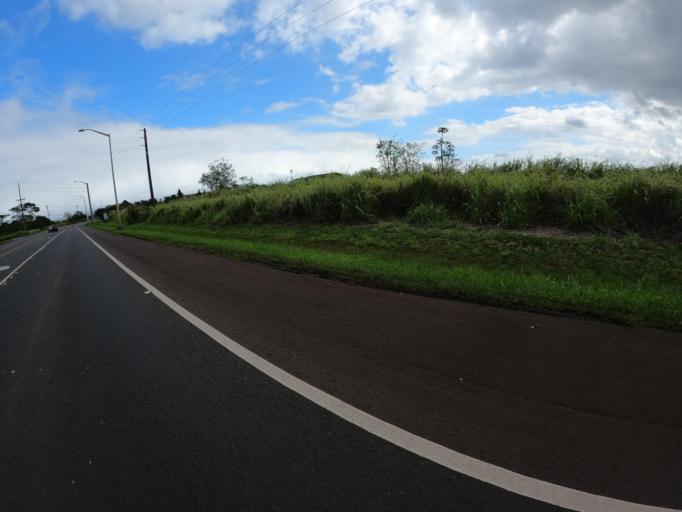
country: US
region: Hawaii
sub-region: Honolulu County
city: Wahiawa
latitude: 21.5077
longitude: -158.0303
